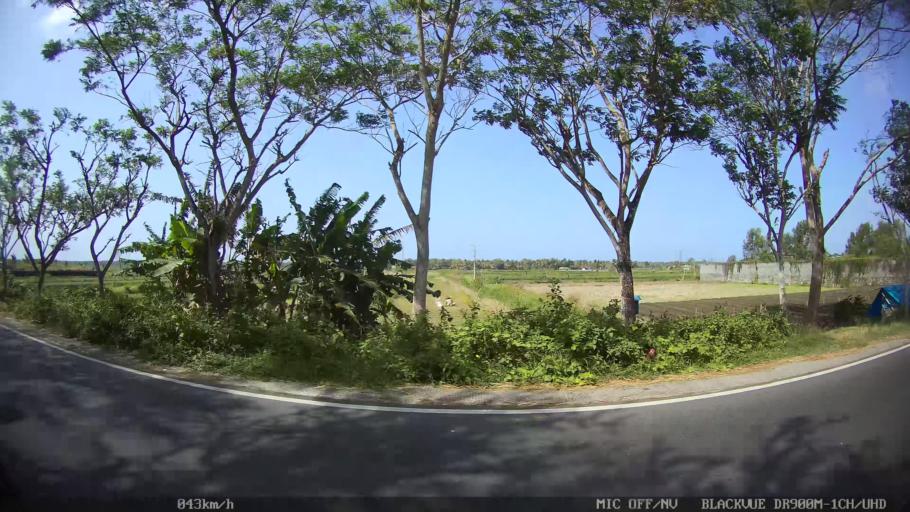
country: ID
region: Daerah Istimewa Yogyakarta
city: Srandakan
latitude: -7.8961
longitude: 110.1554
